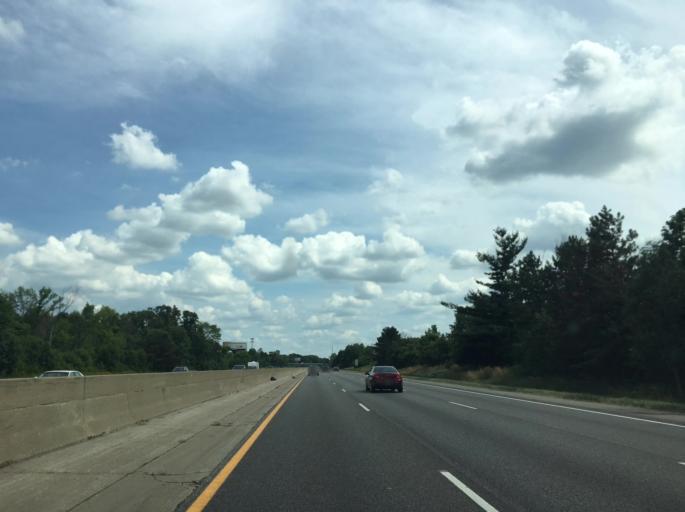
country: US
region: Michigan
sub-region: Genesee County
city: Beecher
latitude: 43.0525
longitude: -83.7589
